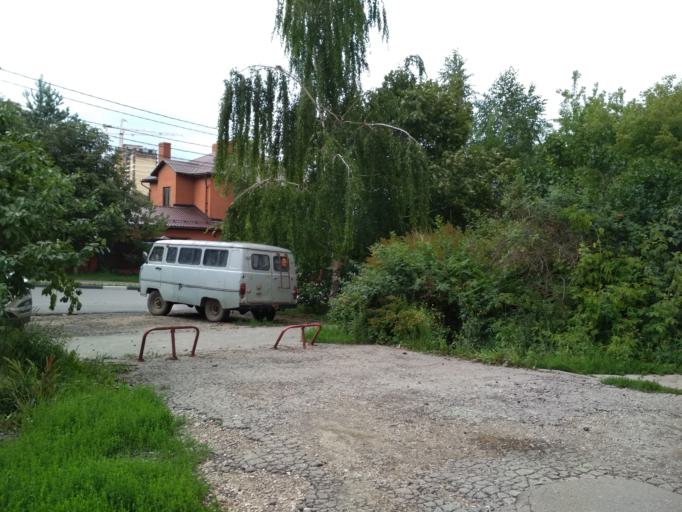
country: RU
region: Tula
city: Mendeleyevskiy
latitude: 54.1541
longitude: 37.5803
